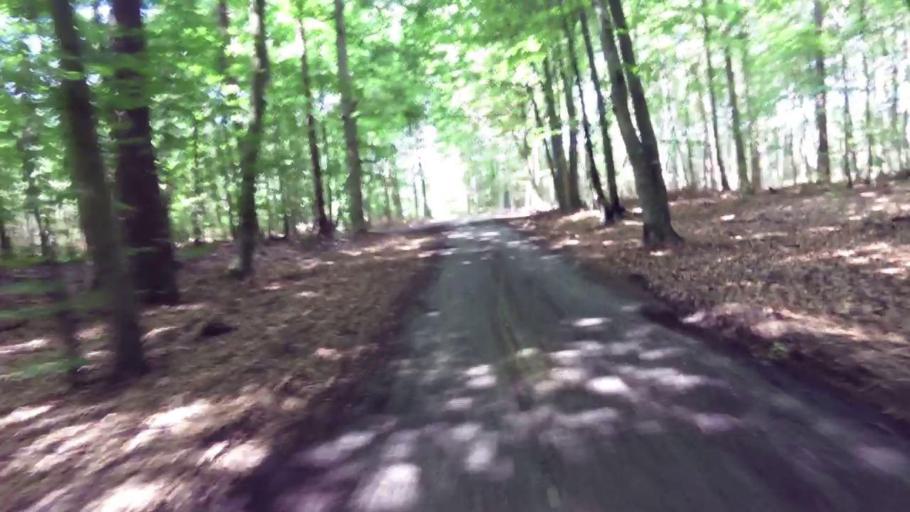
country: PL
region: West Pomeranian Voivodeship
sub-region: Powiat stargardzki
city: Kobylanka
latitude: 53.3476
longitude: 14.8059
